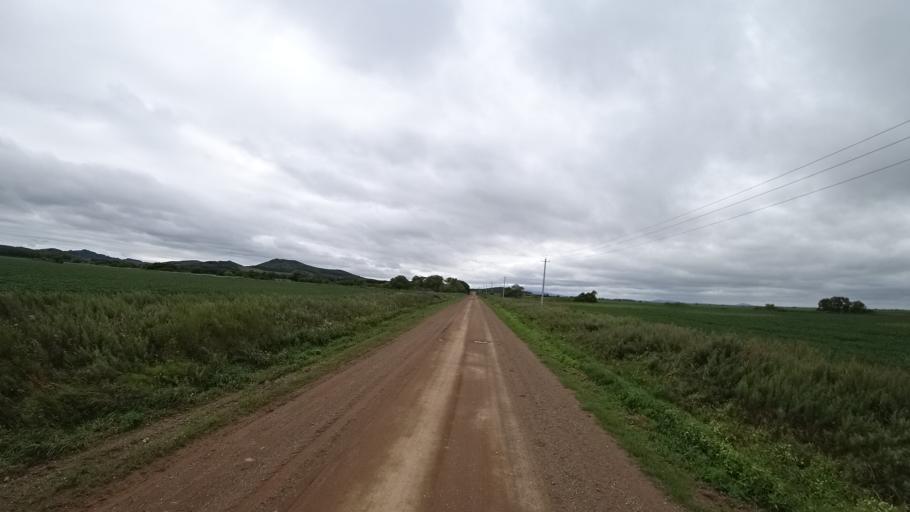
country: RU
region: Primorskiy
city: Chernigovka
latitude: 44.4895
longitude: 132.5724
